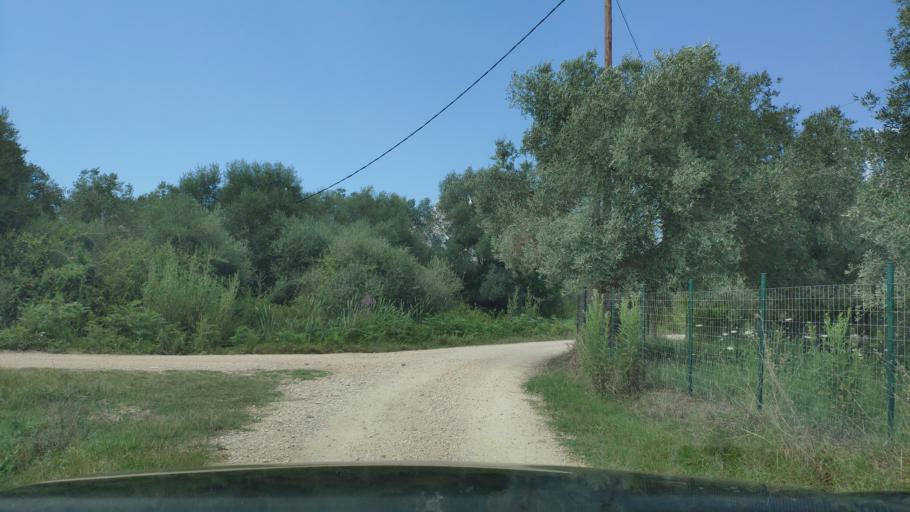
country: GR
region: West Greece
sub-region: Nomos Aitolias kai Akarnanias
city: Menidi
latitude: 39.0593
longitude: 21.0944
